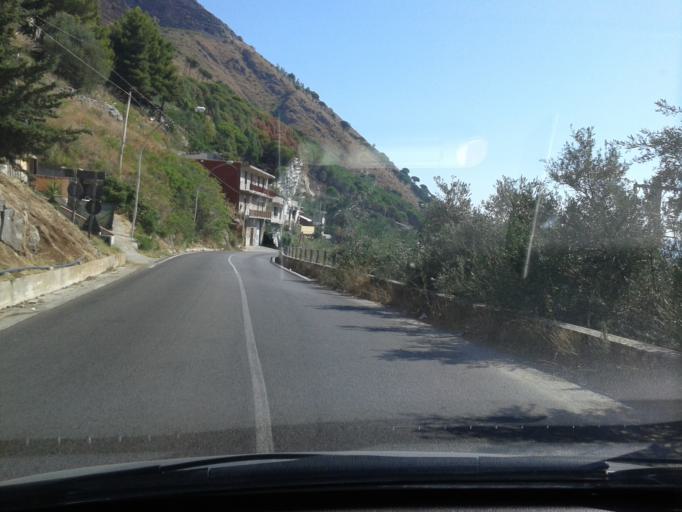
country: IT
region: Sicily
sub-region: Palermo
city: Pioppo
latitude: 38.0500
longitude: 13.2362
